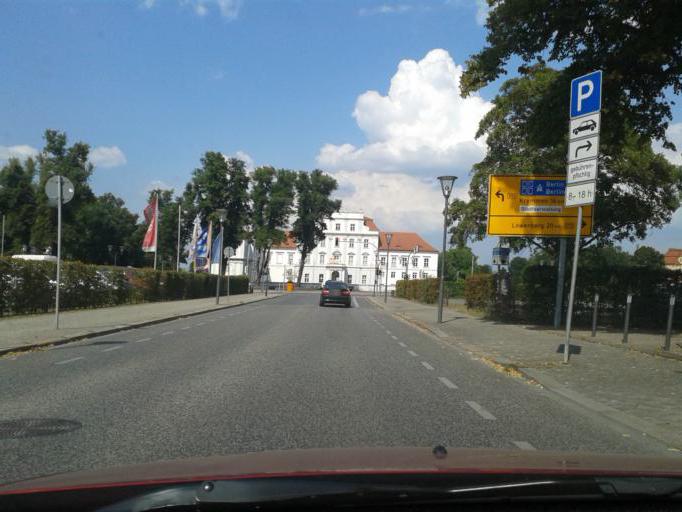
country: DE
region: Brandenburg
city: Oranienburg
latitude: 52.7529
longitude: 13.2368
